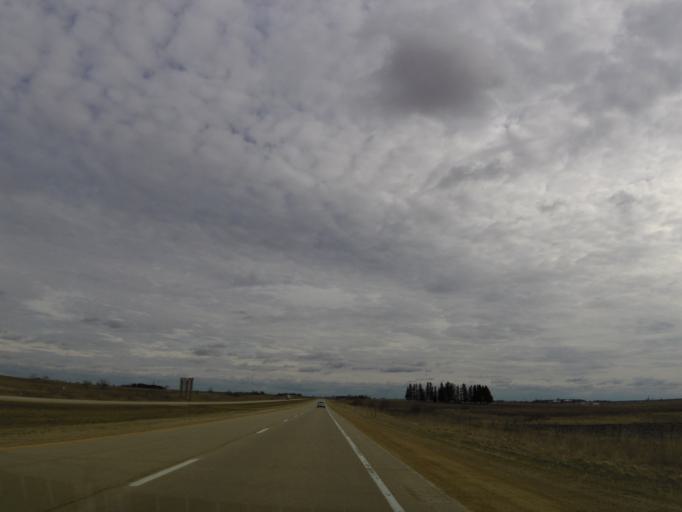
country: US
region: Iowa
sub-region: Chickasaw County
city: New Hampton
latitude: 43.0493
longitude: -92.3350
